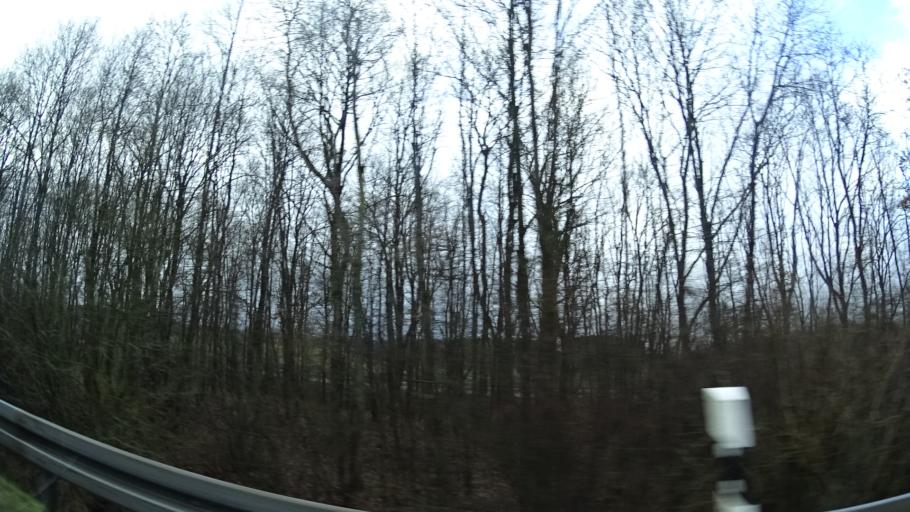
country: DE
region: Hesse
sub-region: Regierungsbezirk Darmstadt
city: Schluchtern
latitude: 50.3912
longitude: 9.5367
